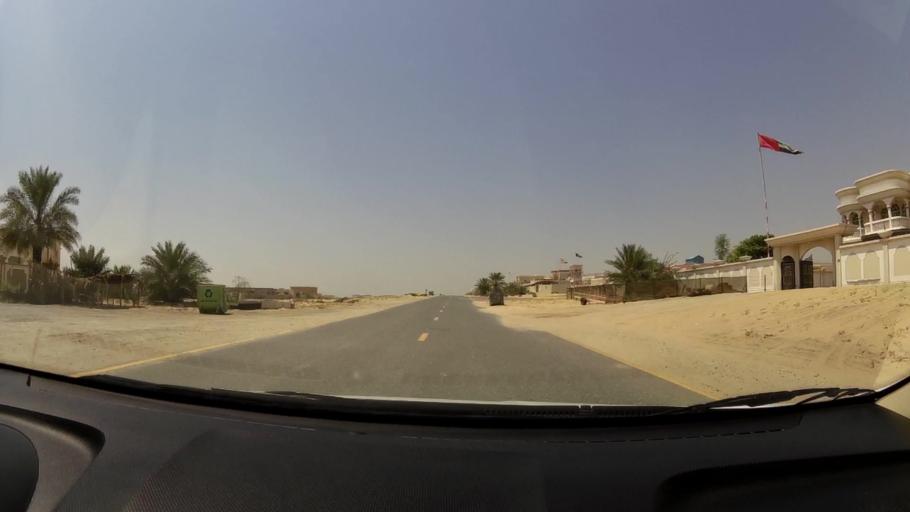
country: AE
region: Umm al Qaywayn
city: Umm al Qaywayn
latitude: 25.5070
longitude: 55.5835
